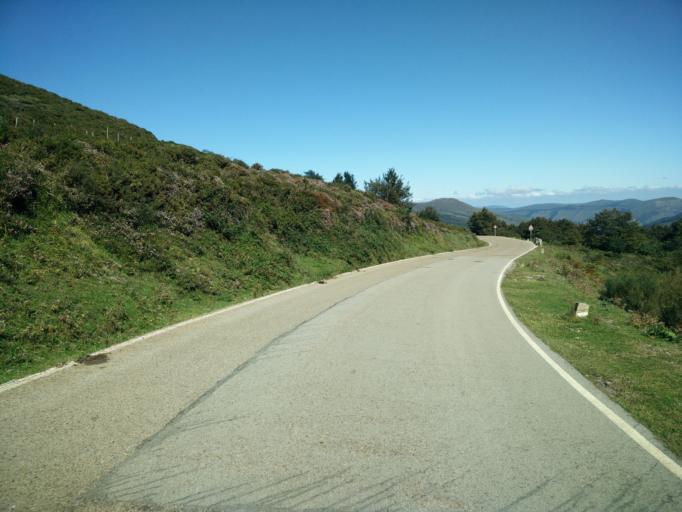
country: ES
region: Cantabria
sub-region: Provincia de Cantabria
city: Reinosa
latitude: 43.0658
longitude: -4.2328
